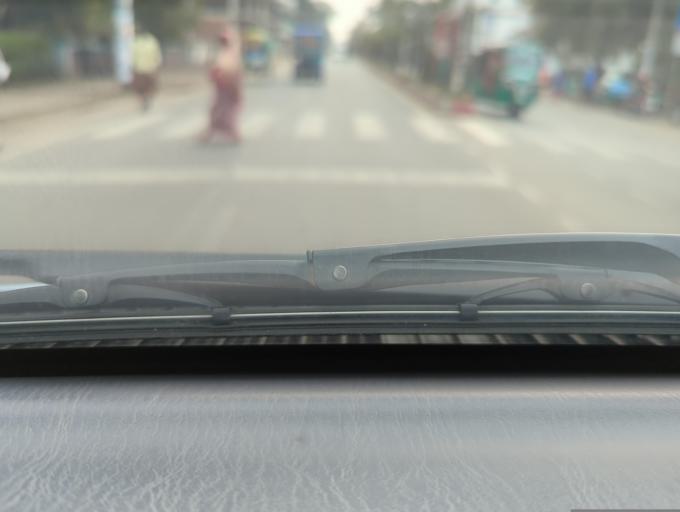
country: BD
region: Sylhet
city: Maulavi Bazar
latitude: 24.4827
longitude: 91.7655
